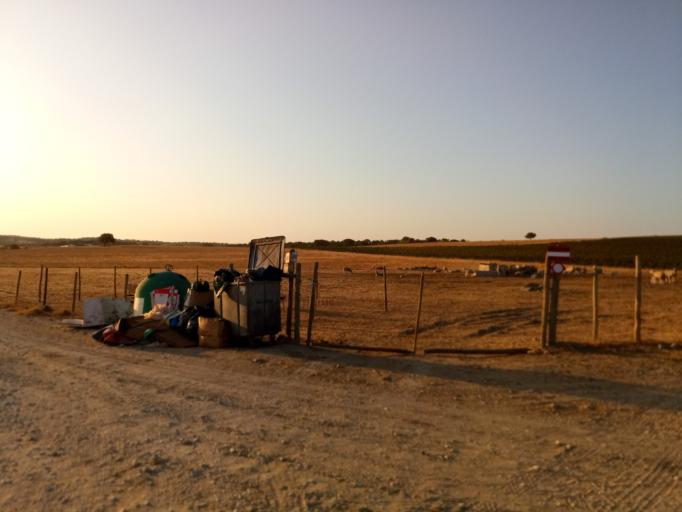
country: PT
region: Evora
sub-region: Reguengos de Monsaraz
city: Reguengos de Monsaraz
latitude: 38.3821
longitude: -7.4512
